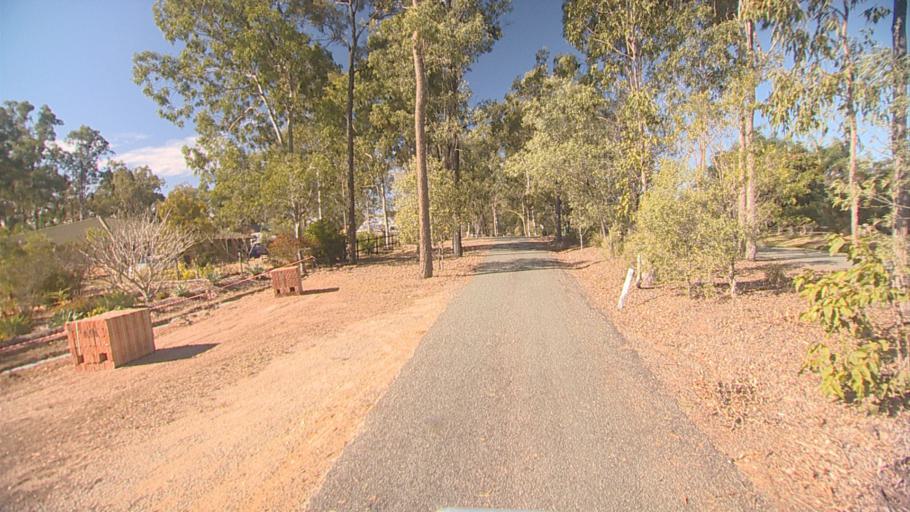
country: AU
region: Queensland
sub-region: Ipswich
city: Springfield Lakes
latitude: -27.7344
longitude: 152.9256
